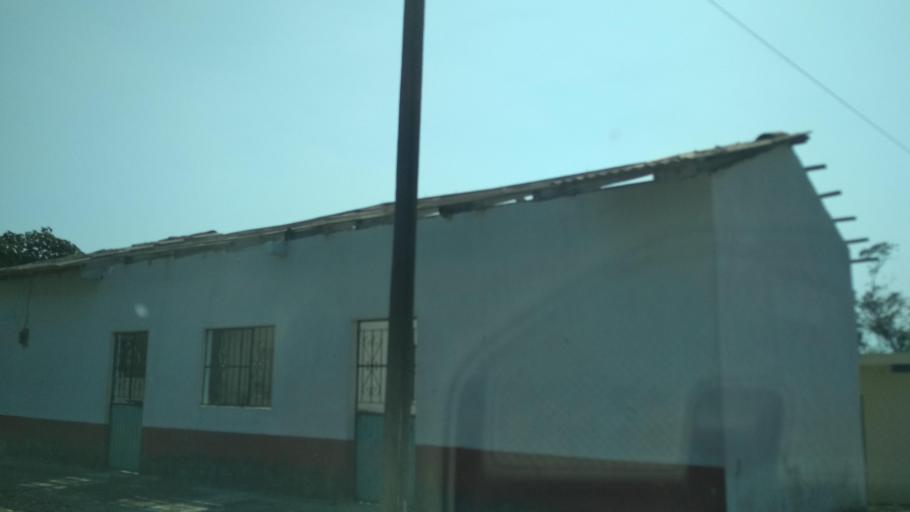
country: MX
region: Veracruz
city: Gutierrez Zamora
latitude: 20.4250
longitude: -97.1905
